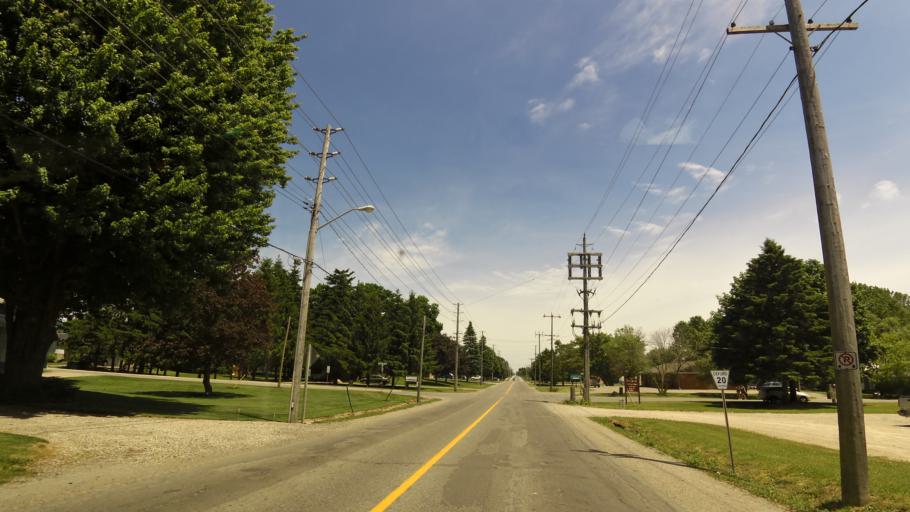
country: CA
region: Ontario
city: Ingersoll
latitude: 42.8785
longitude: -80.7447
